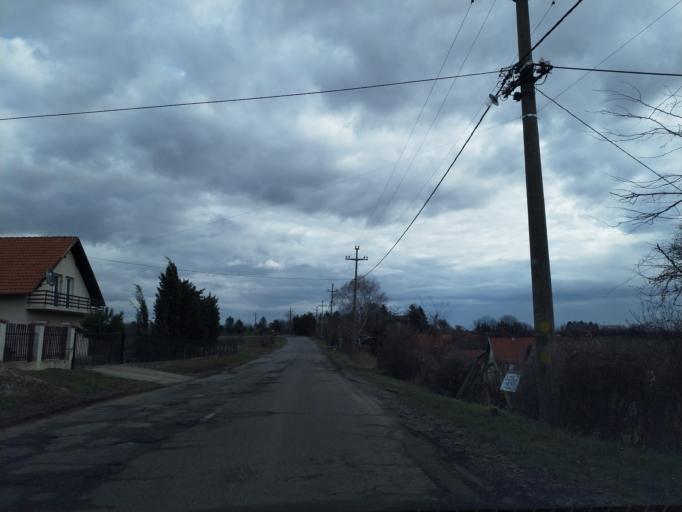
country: RS
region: Central Serbia
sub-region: Belgrade
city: Grocka
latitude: 44.6202
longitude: 20.7386
